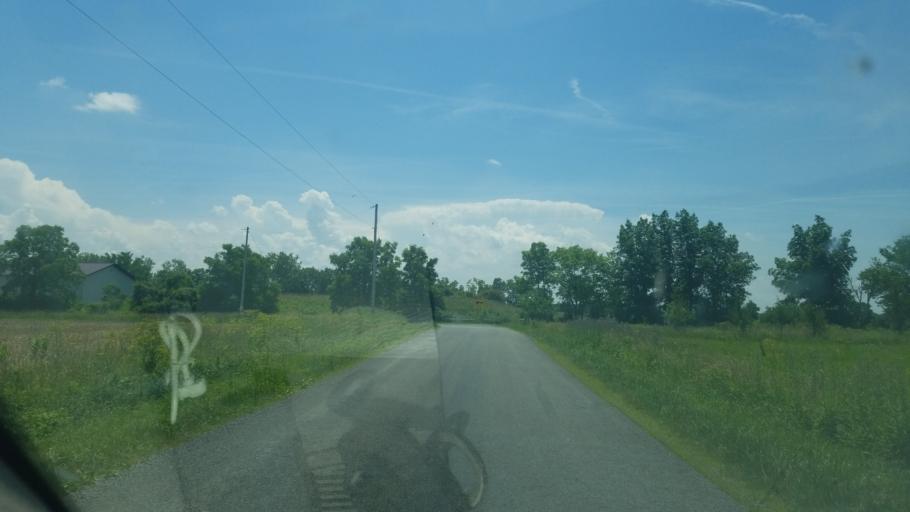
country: US
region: Ohio
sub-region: Hancock County
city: Findlay
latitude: 40.9942
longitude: -83.6362
